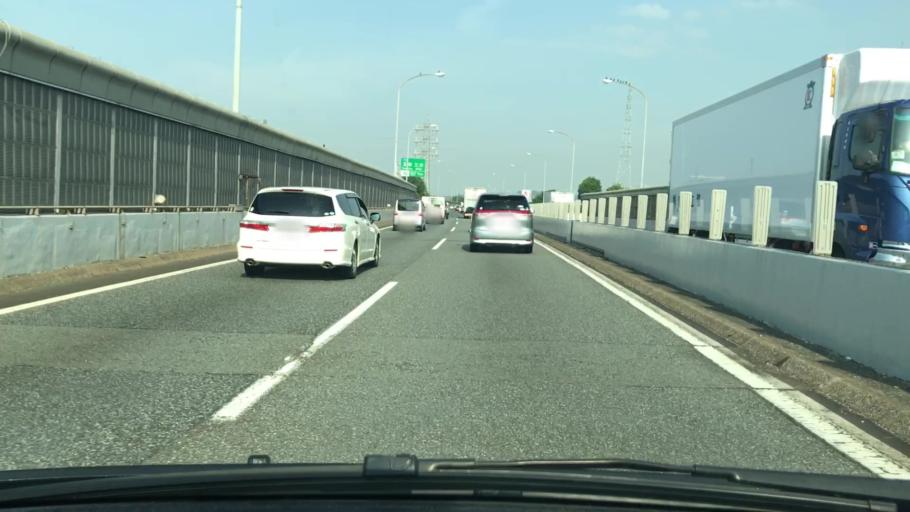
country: JP
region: Hyogo
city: Akashi
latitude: 34.6829
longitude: 134.9920
